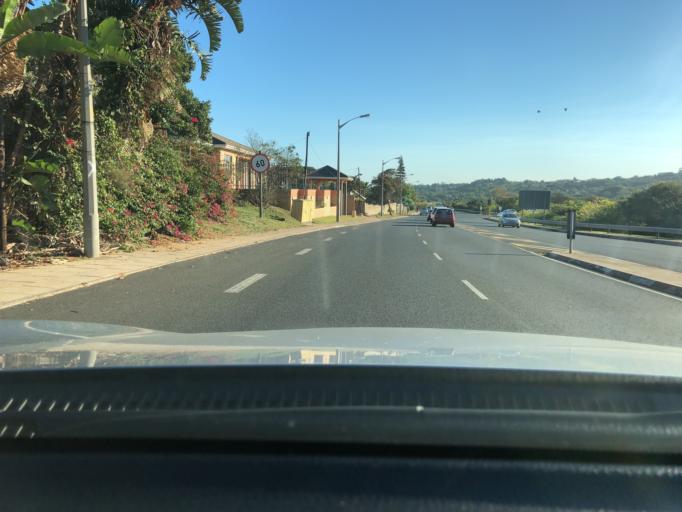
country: ZA
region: KwaZulu-Natal
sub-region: eThekwini Metropolitan Municipality
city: Umkomaas
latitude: -30.0390
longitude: 30.8976
